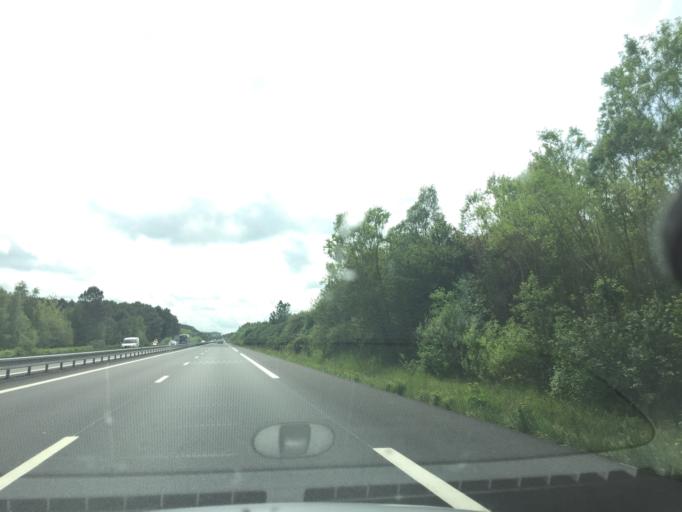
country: FR
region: Pays de la Loire
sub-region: Departement de la Sarthe
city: Brette-les-Pins
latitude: 47.9338
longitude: 0.3103
